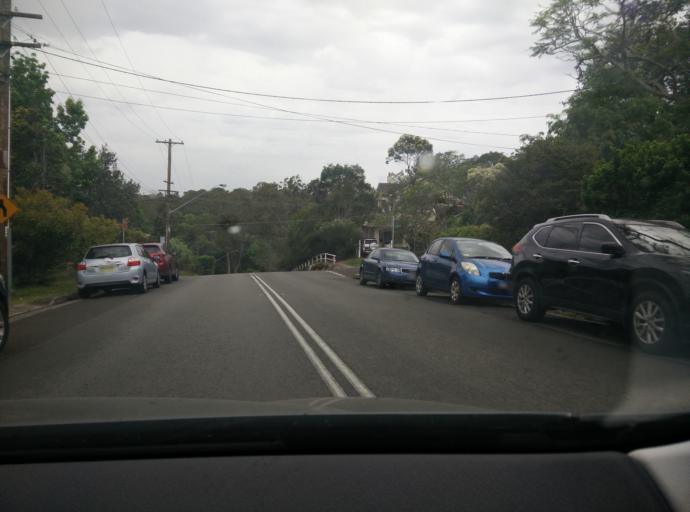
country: AU
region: New South Wales
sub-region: Ku-ring-gai
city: Lindfield
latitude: -33.7733
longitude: 151.1742
